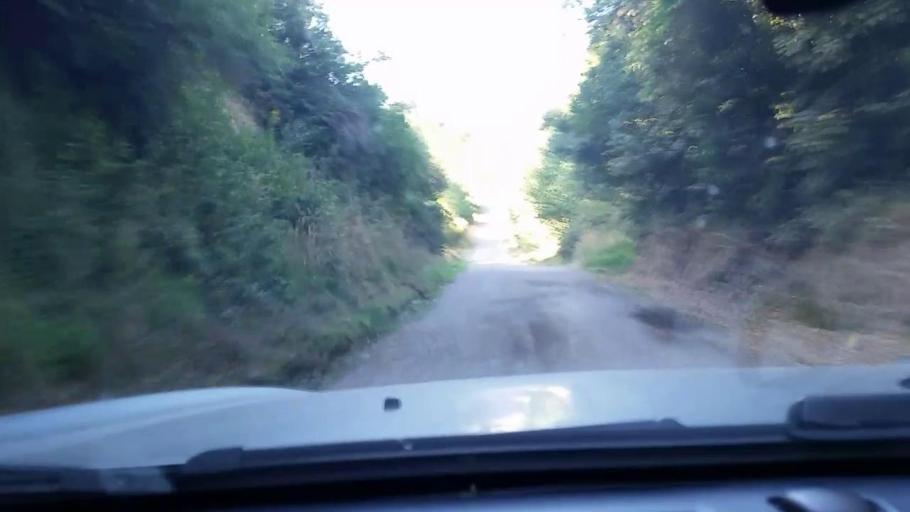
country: NZ
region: Waikato
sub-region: Taupo District
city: Taupo
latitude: -38.4849
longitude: 176.2112
